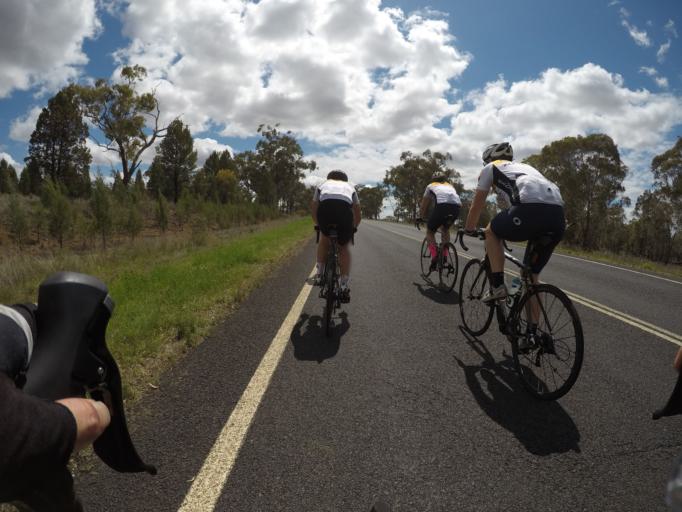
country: AU
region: New South Wales
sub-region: Dubbo Municipality
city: Dubbo
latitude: -32.4469
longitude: 148.5831
